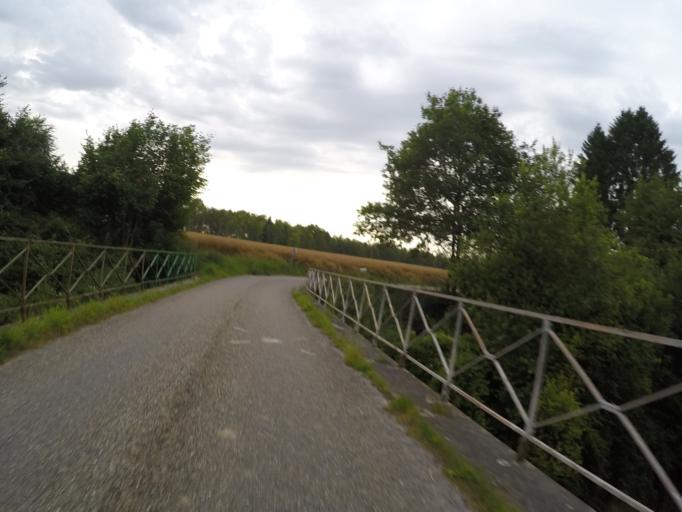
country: BE
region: Wallonia
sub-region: Province de Namur
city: Assesse
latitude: 50.3171
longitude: 5.0382
